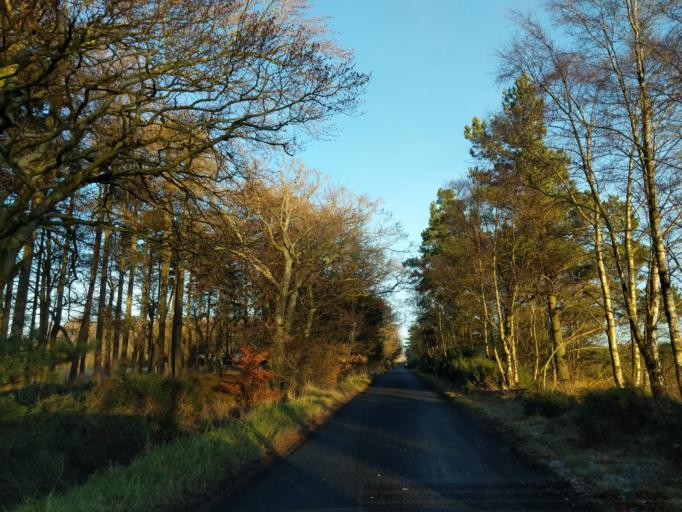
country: GB
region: Scotland
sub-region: Edinburgh
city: Balerno
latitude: 55.8634
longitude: -3.3364
